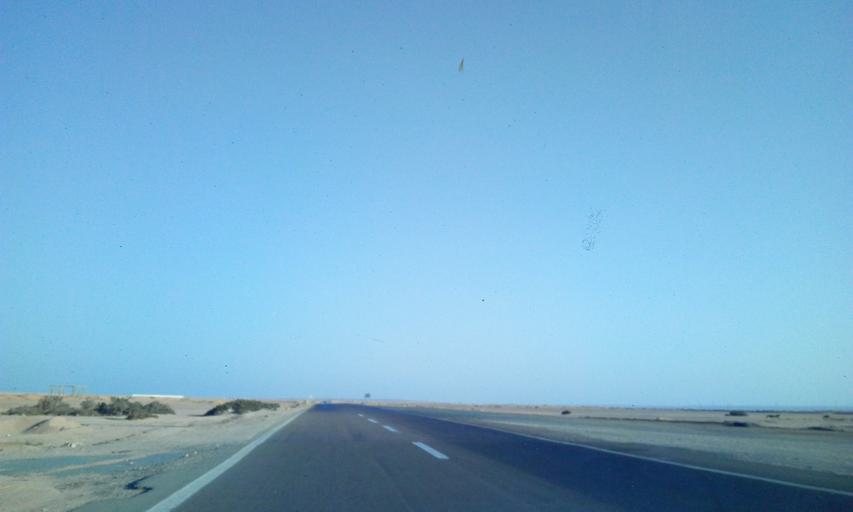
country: EG
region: South Sinai
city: Tor
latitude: 28.4487
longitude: 32.9967
